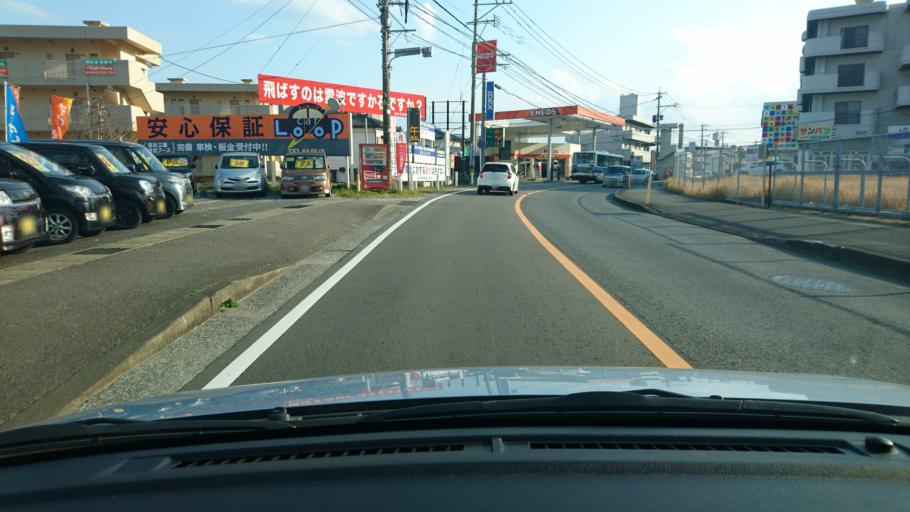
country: JP
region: Miyazaki
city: Miyazaki-shi
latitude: 31.8830
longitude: 131.4083
